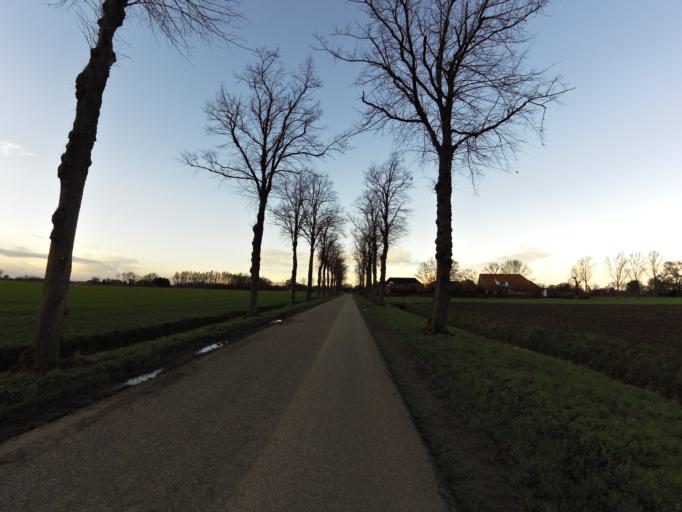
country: NL
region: Gelderland
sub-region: Oude IJsselstreek
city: Gendringen
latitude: 51.8483
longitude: 6.3685
